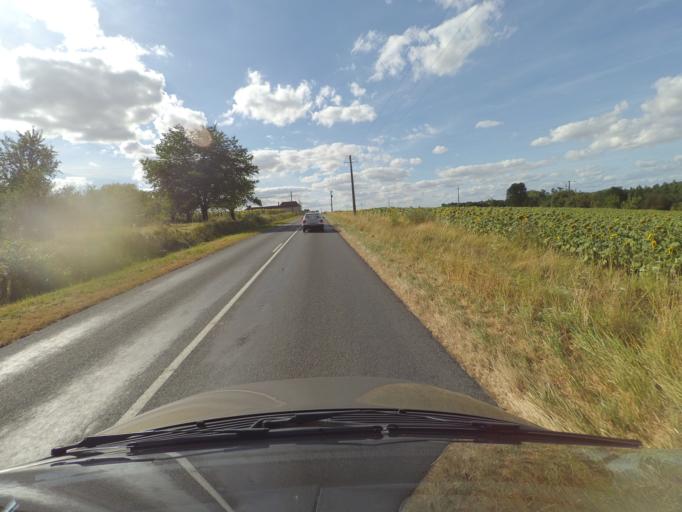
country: FR
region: Poitou-Charentes
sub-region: Departement de la Vienne
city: Saint-Gervais-les-Trois-Clochers
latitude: 46.9528
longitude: 0.4057
